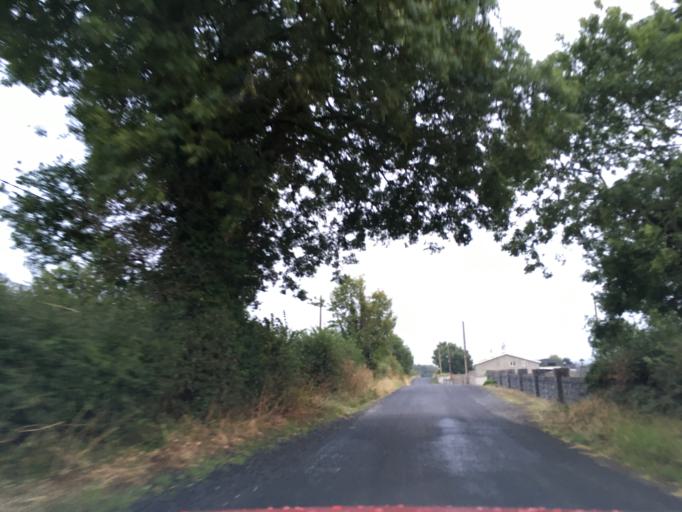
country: IE
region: Munster
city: Cahir
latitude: 52.4634
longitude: -7.9734
